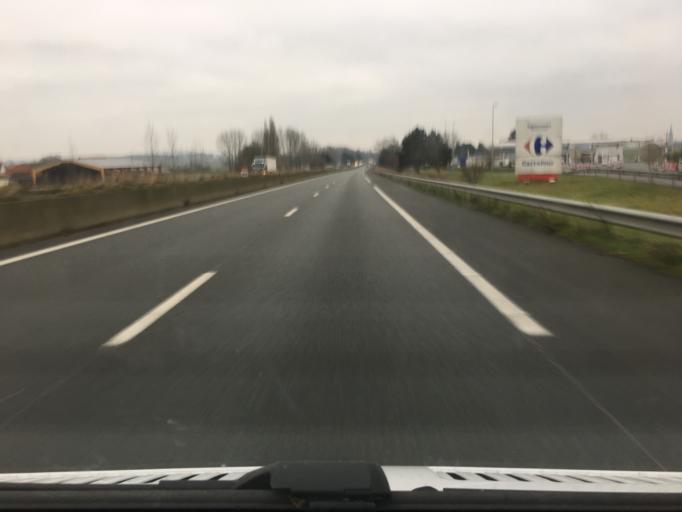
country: FR
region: Nord-Pas-de-Calais
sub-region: Departement du Nord
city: Steenvoorde
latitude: 50.8320
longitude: 2.5792
